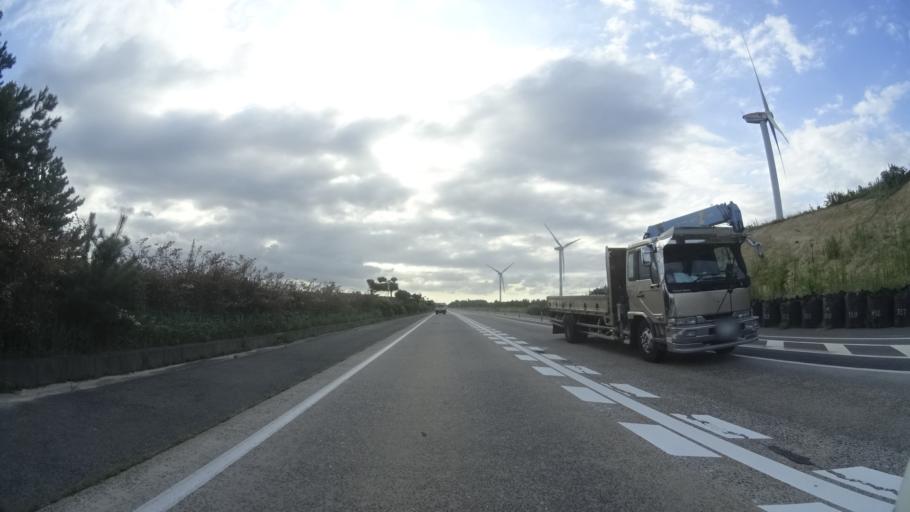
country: JP
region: Tottori
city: Kurayoshi
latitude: 35.4985
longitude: 133.8016
